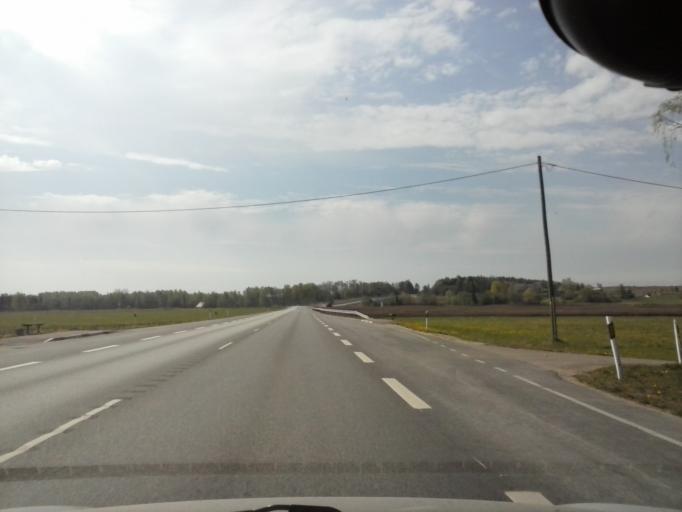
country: EE
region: Tartu
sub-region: UElenurme vald
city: Ulenurme
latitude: 58.2120
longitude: 26.7057
